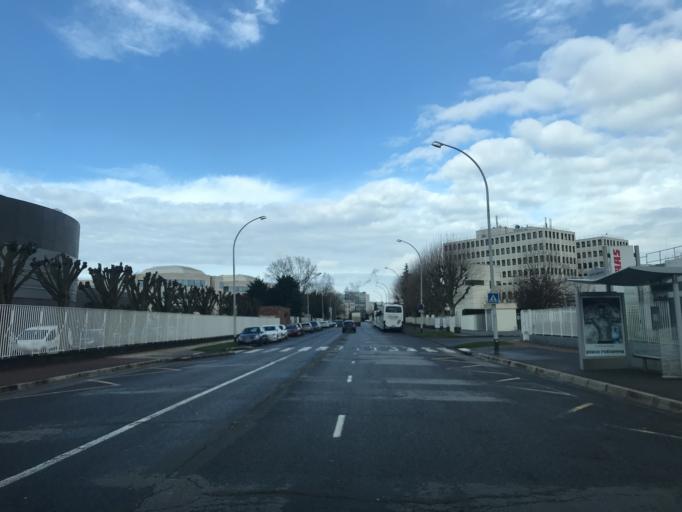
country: FR
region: Ile-de-France
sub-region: Departement des Yvelines
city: Velizy-Villacoublay
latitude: 48.7826
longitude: 2.2180
